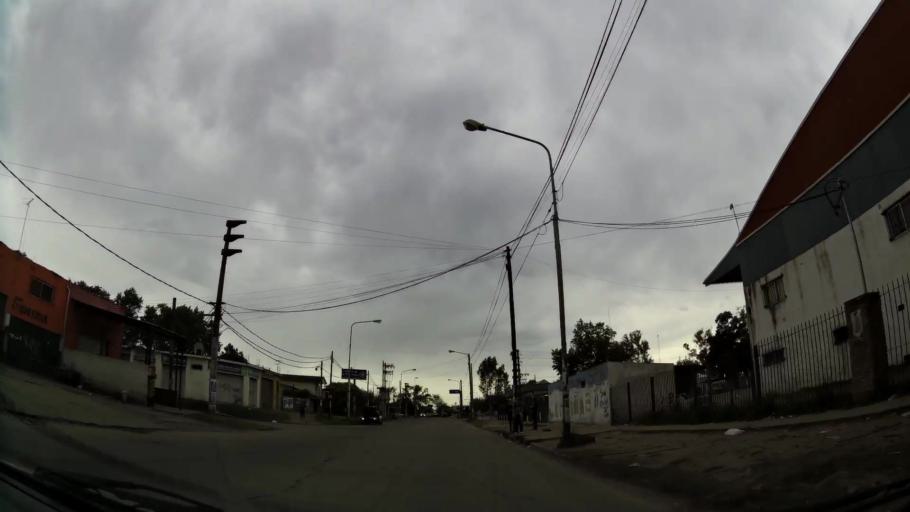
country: AR
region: Buenos Aires
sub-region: Partido de Quilmes
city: Quilmes
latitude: -34.7876
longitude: -58.2577
